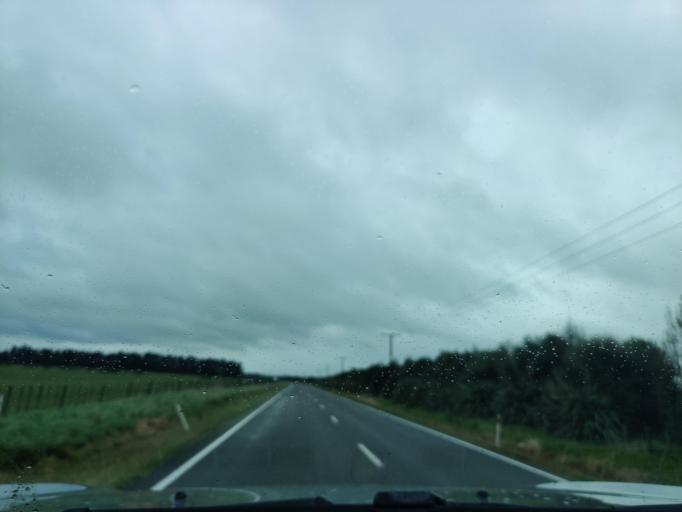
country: NZ
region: Hawke's Bay
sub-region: Hastings District
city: Hastings
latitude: -40.0077
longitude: 176.3840
